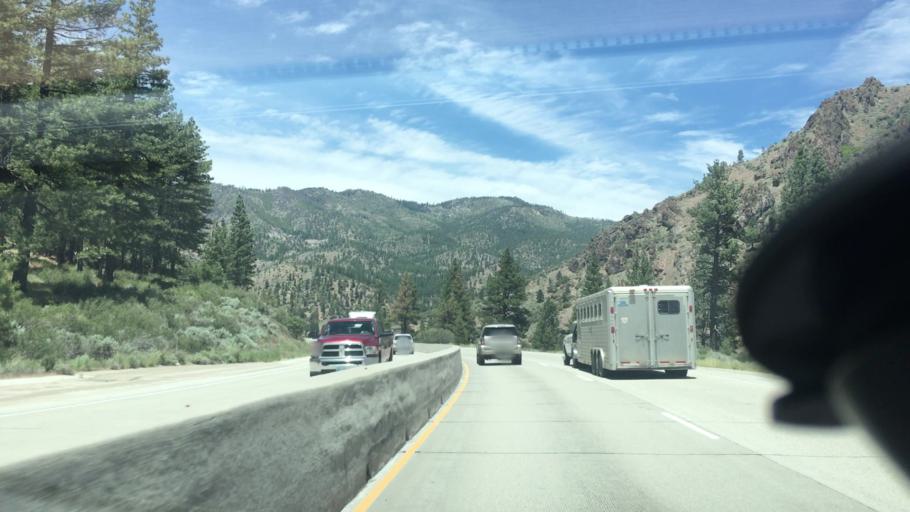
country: US
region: Nevada
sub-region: Washoe County
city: Verdi
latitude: 39.4144
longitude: -120.0287
